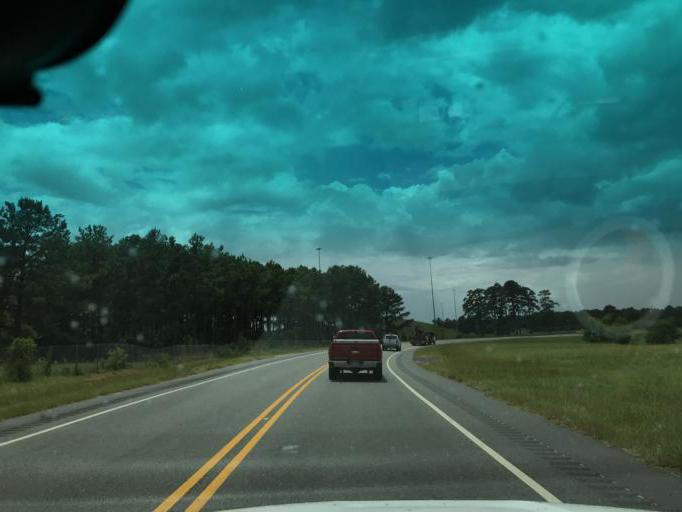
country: US
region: Alabama
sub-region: Montgomery County
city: Pike Road
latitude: 32.3698
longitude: -86.0797
